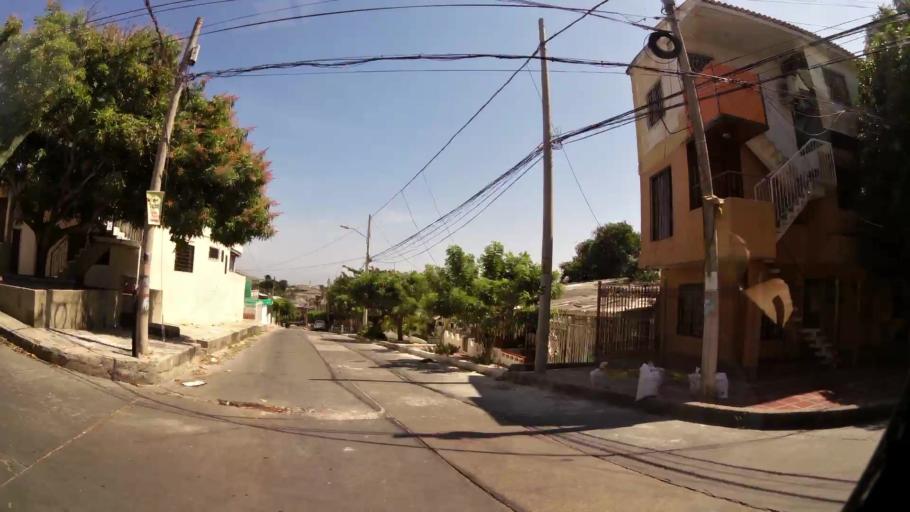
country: CO
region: Atlantico
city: Barranquilla
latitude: 10.9795
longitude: -74.7983
